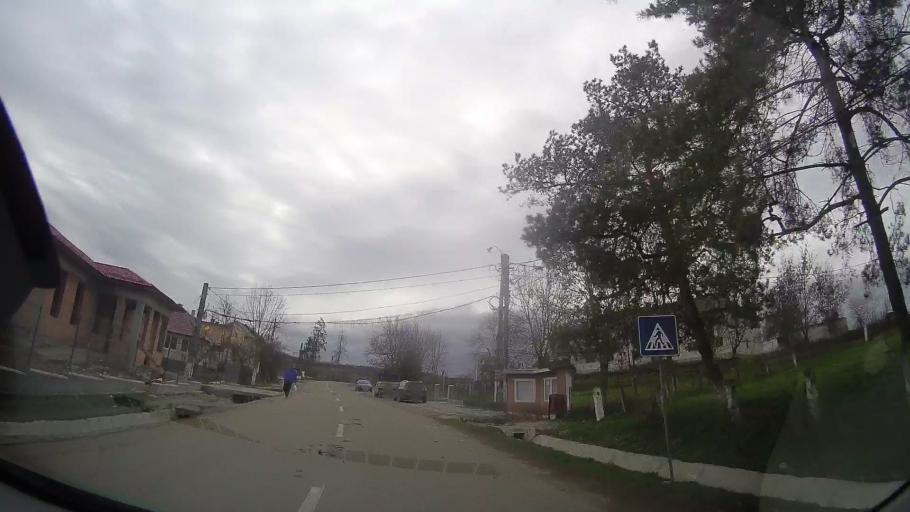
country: RO
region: Bistrita-Nasaud
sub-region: Comuna Milas
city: Milas
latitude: 46.8178
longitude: 24.4375
